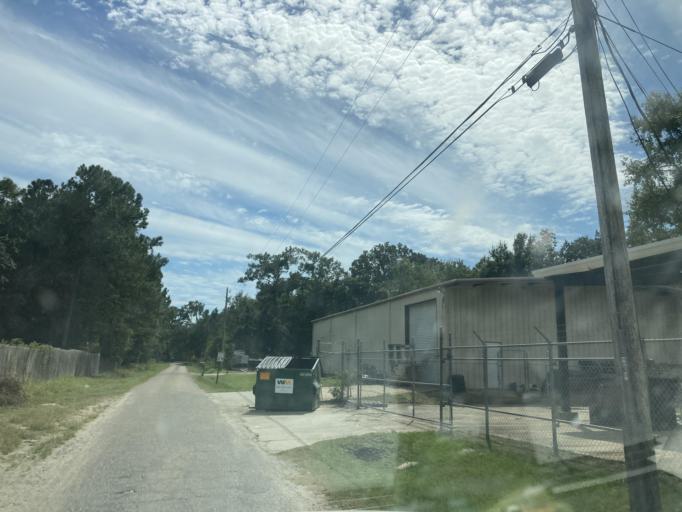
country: US
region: Mississippi
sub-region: Harrison County
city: D'Iberville
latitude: 30.4368
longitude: -88.8819
